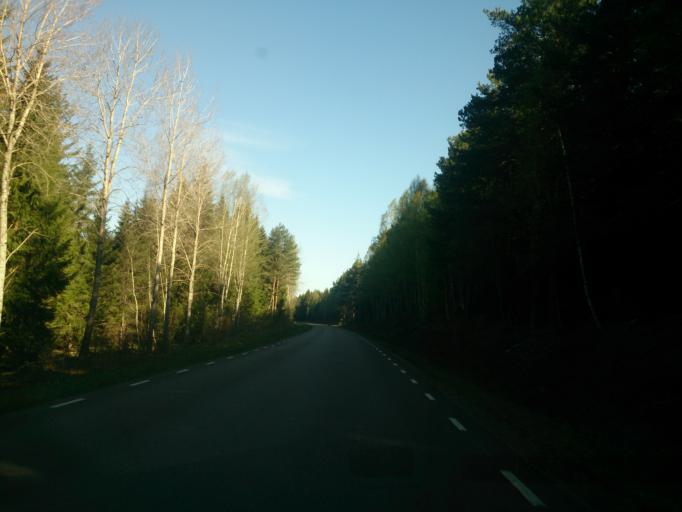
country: SE
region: OEstergoetland
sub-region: Linkopings Kommun
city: Ljungsbro
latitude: 58.5929
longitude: 15.5002
